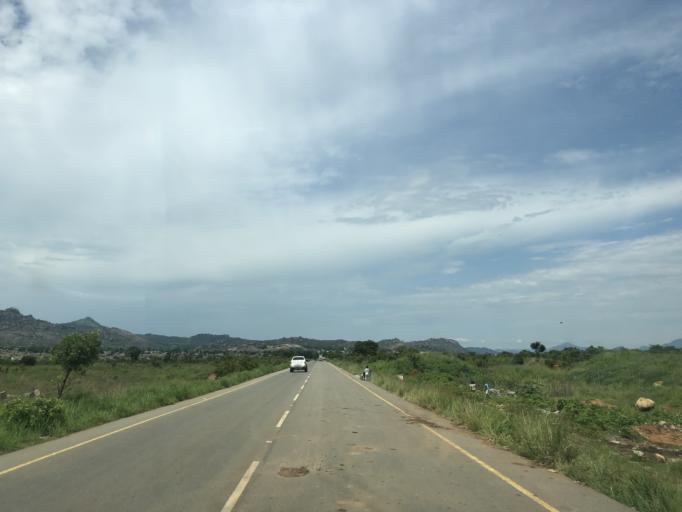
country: AO
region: Cuanza Sul
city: Quibala
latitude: -10.7345
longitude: 15.0057
